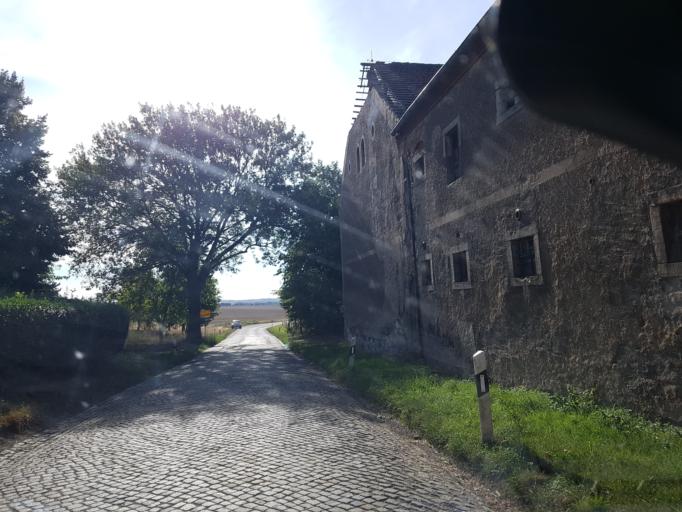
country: DE
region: Saxony
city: Naundorf
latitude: 51.2283
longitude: 13.1321
